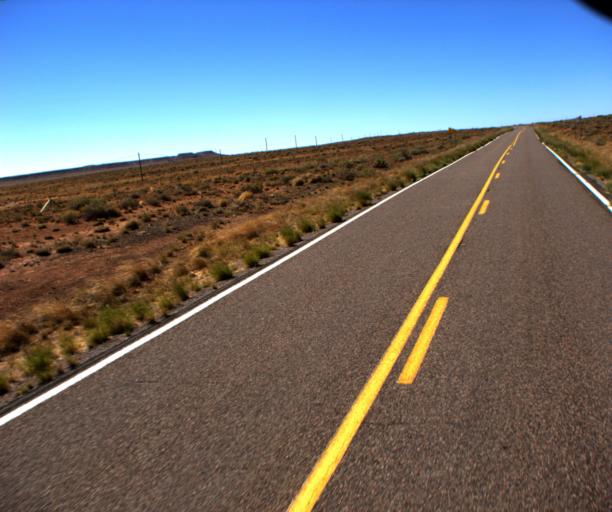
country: US
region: Arizona
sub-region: Coconino County
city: LeChee
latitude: 35.1047
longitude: -110.8642
